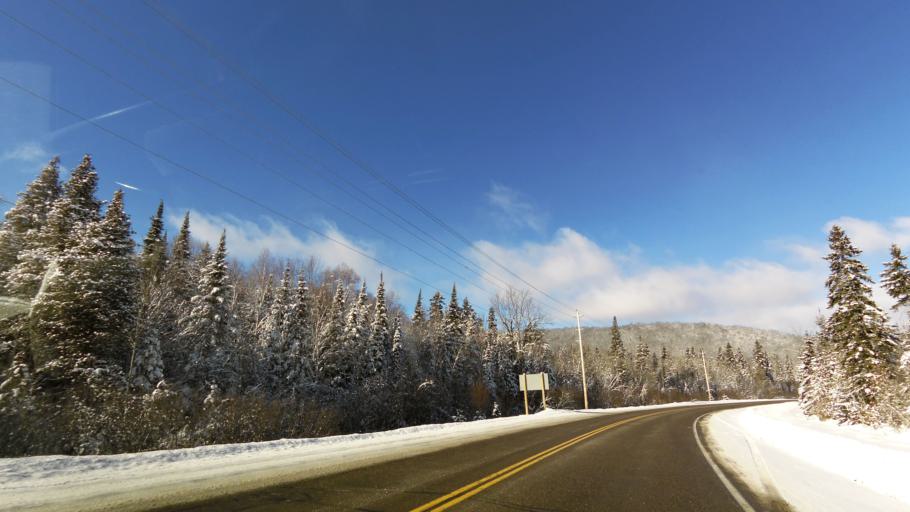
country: CA
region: Ontario
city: Bancroft
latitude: 44.9749
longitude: -78.2780
